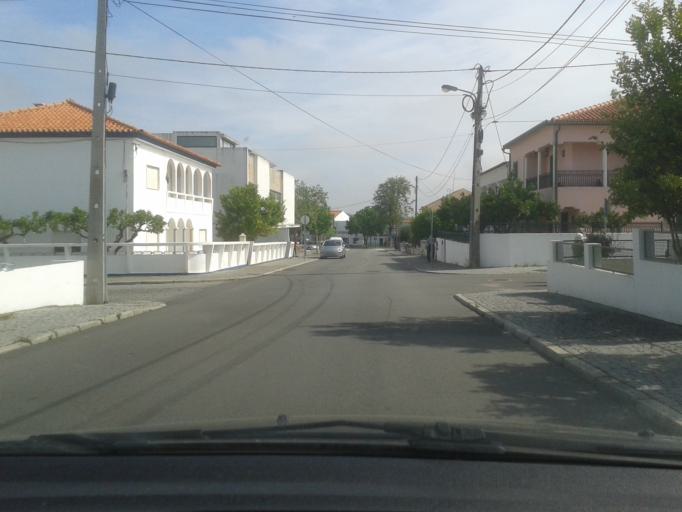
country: PT
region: Portalegre
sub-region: Avis
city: Avis
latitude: 39.0516
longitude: -7.8890
